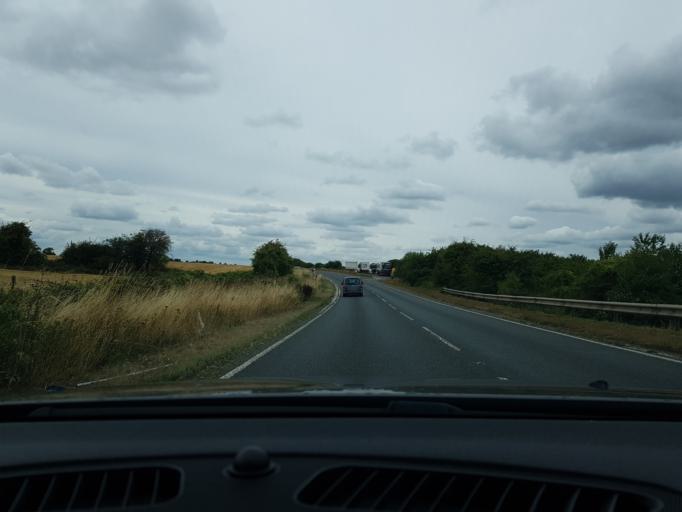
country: GB
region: England
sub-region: Hampshire
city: Basingstoke
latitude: 51.2832
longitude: -1.1324
